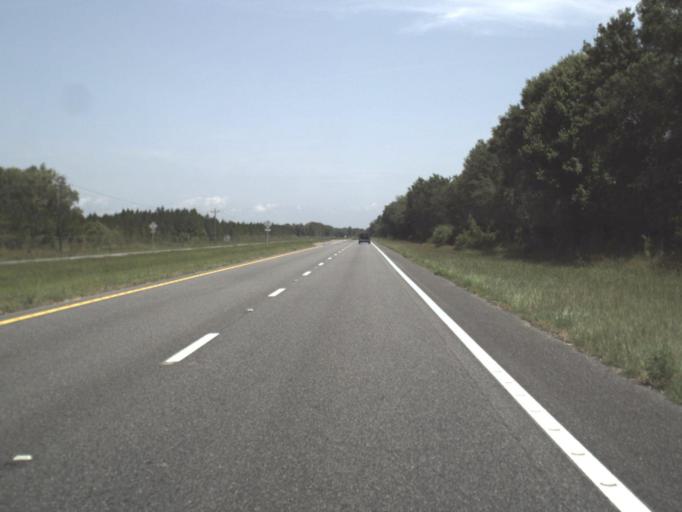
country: US
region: Florida
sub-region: Taylor County
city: Steinhatchee
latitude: 29.8020
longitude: -83.3395
